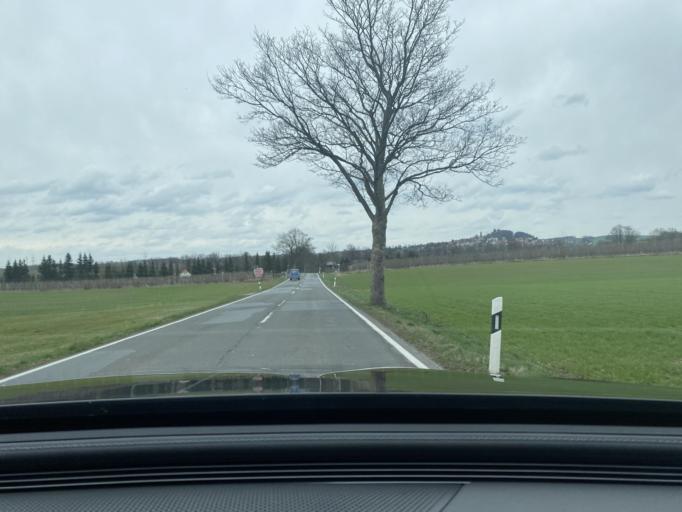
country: DE
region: Saxony
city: Stolpen
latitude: 51.0359
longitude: 14.0487
